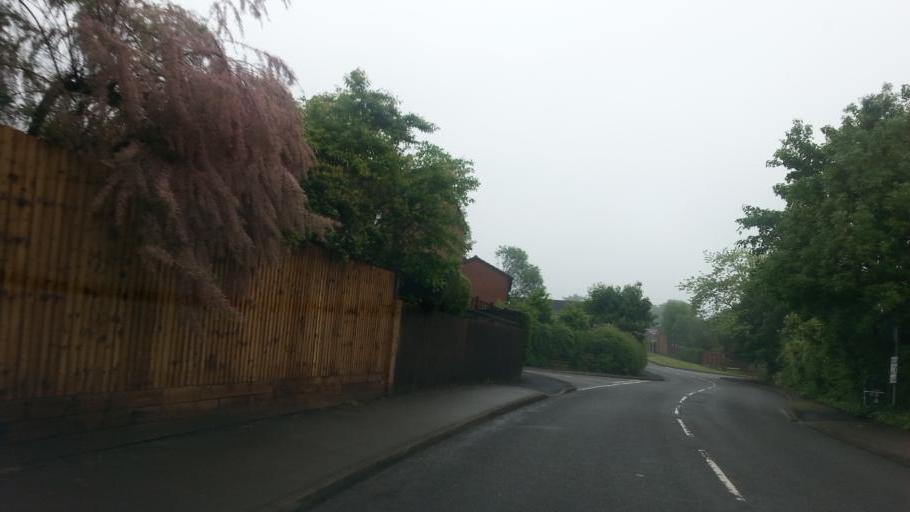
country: GB
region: England
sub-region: Leicestershire
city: Oadby
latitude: 52.5938
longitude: -1.0625
